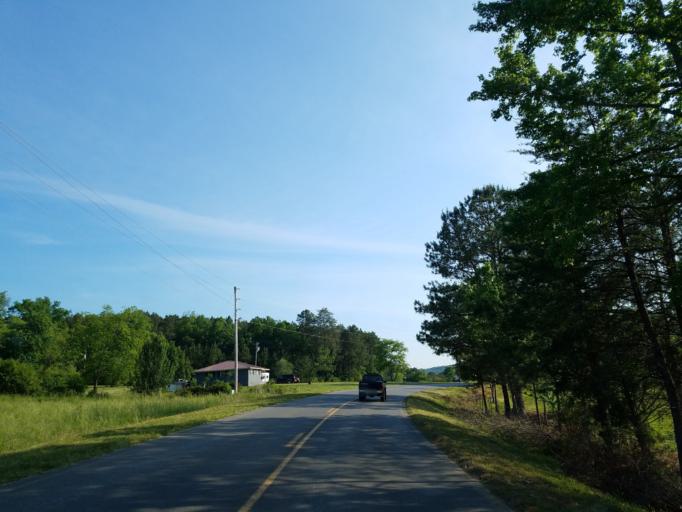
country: US
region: Georgia
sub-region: Chattooga County
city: Trion
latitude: 34.5706
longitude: -85.1559
